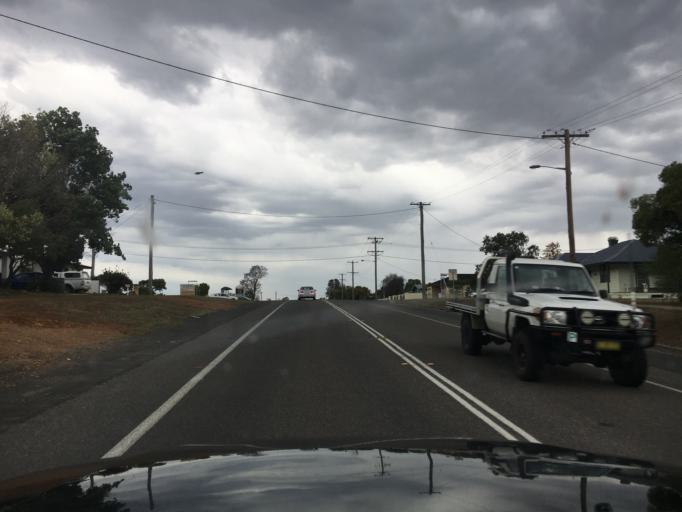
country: AU
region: New South Wales
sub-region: Muswellbrook
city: Muswellbrook
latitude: -32.1713
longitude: 150.8908
